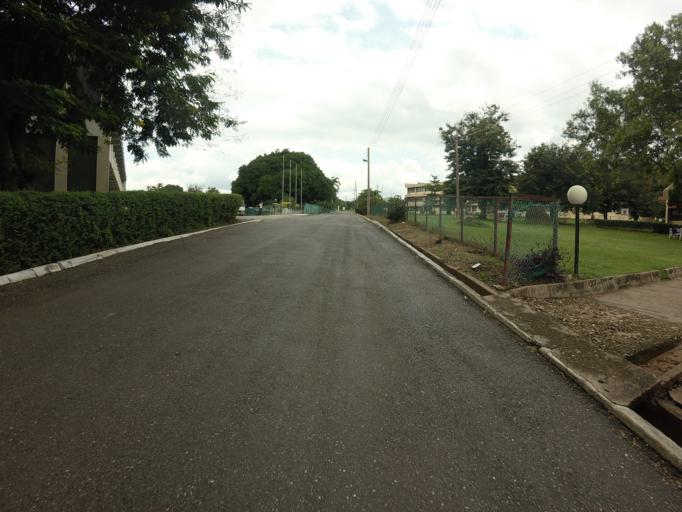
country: GH
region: Volta
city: Ho
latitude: 6.5910
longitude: 0.4683
